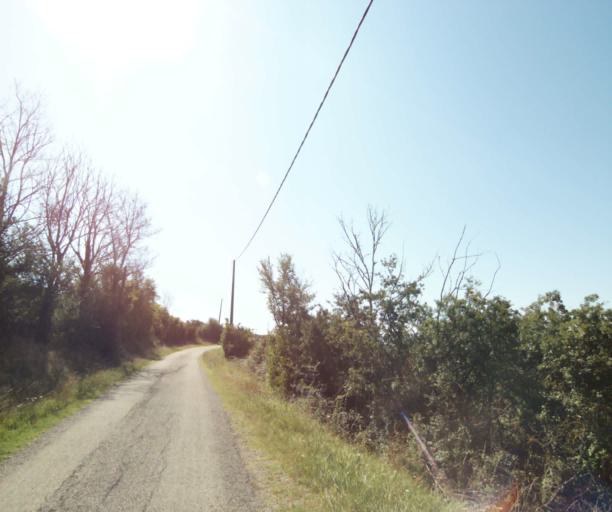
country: FR
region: Midi-Pyrenees
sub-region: Departement de l'Ariege
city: Lezat-sur-Leze
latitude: 43.2481
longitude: 1.3741
